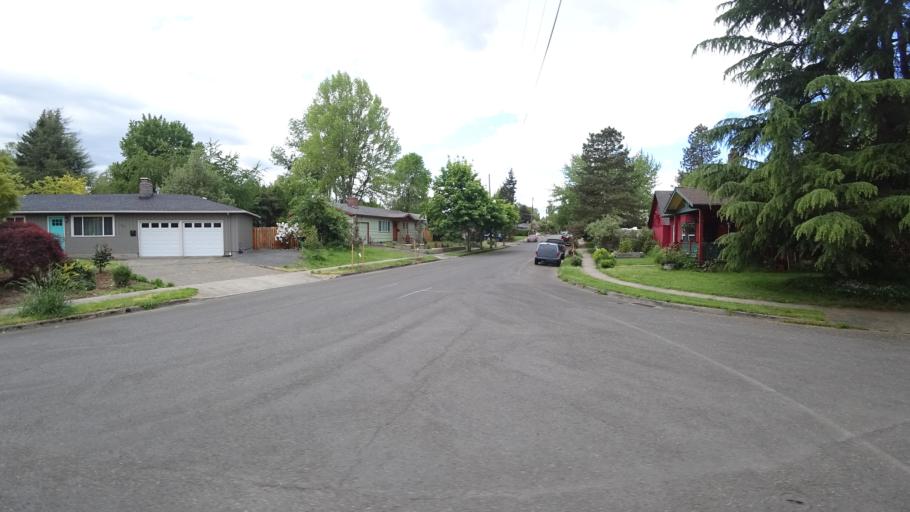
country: US
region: Oregon
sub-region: Washington County
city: Beaverton
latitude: 45.4786
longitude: -122.7932
